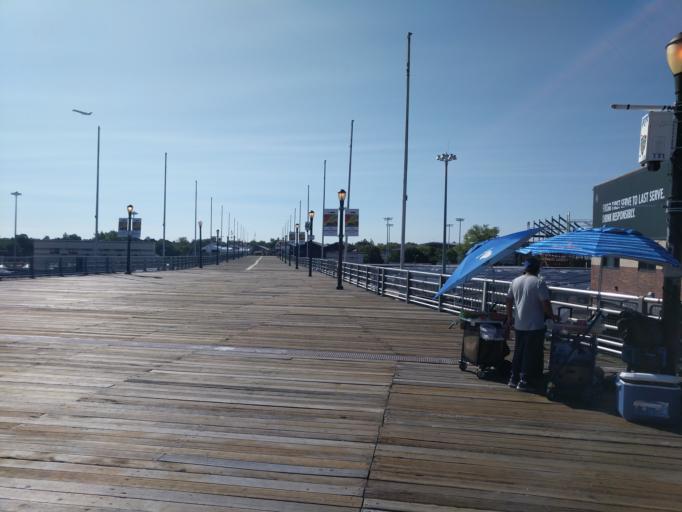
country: US
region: New York
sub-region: Queens County
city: Borough of Queens
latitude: 40.7539
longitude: -73.8454
